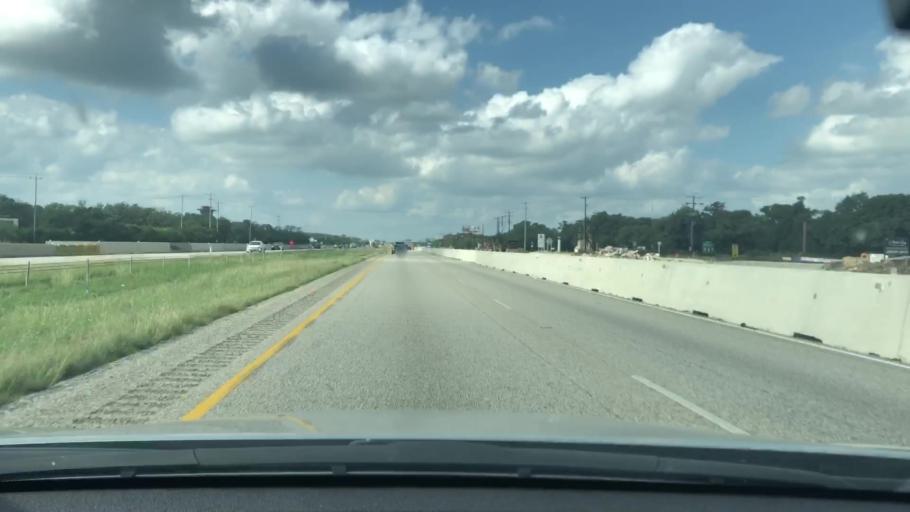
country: US
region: Texas
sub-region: Bexar County
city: Cross Mountain
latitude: 29.6794
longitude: -98.6381
